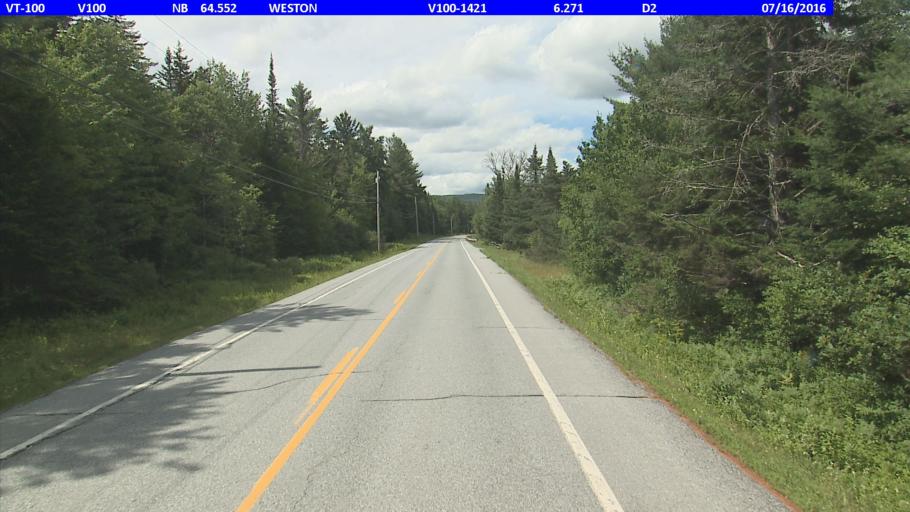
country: US
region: Vermont
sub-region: Windsor County
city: Chester
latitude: 43.3330
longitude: -72.7839
